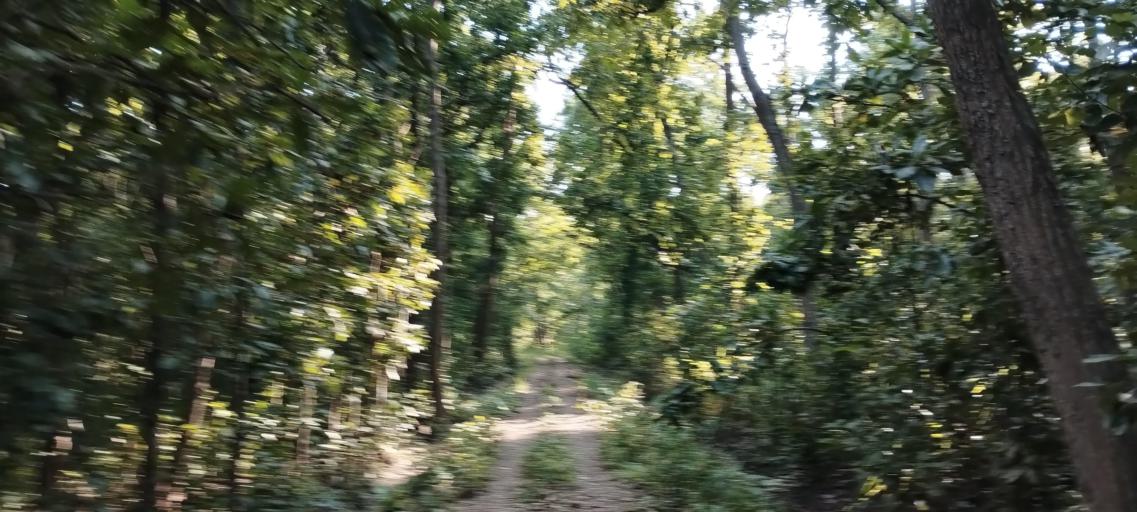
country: NP
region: Far Western
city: Tikapur
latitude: 28.5066
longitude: 81.2667
